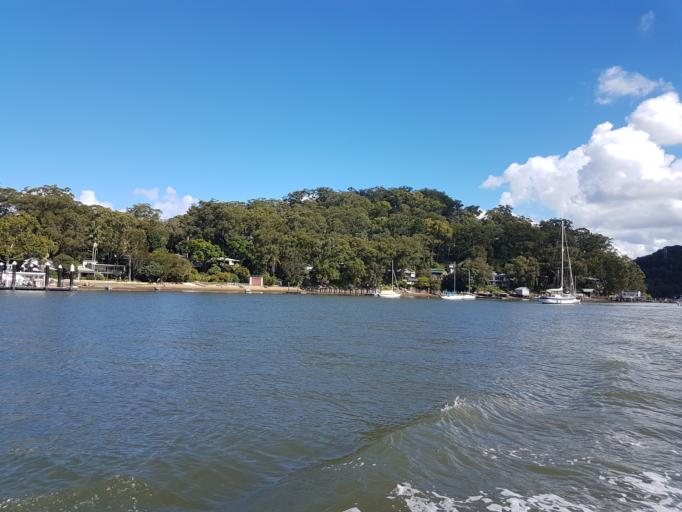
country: AU
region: New South Wales
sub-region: Gosford Shire
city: Umina
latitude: -33.5352
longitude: 151.2411
